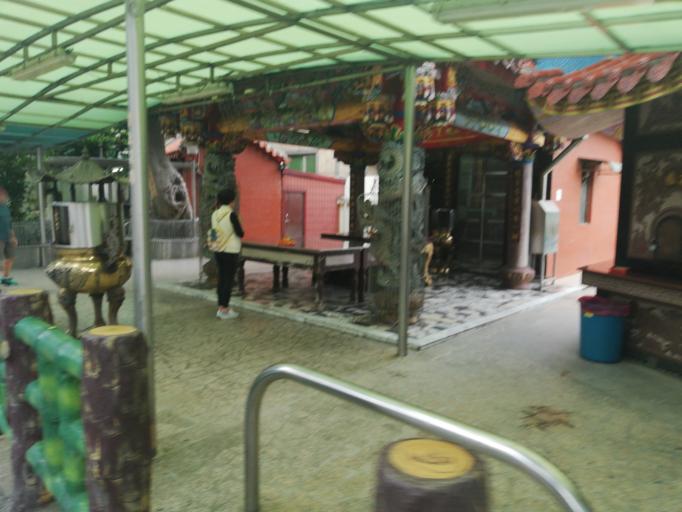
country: TW
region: Taiwan
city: Taoyuan City
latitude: 25.0089
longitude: 121.3023
